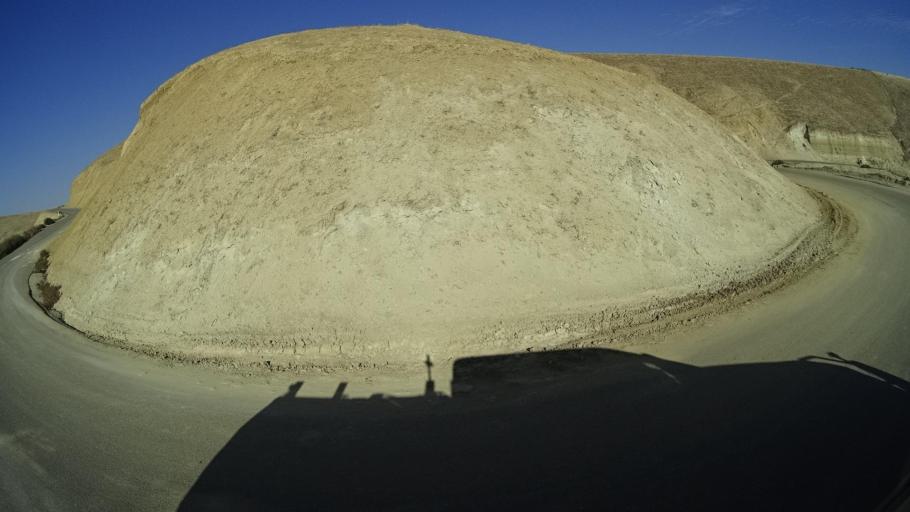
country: US
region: California
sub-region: Kern County
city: Oildale
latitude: 35.4713
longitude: -118.8710
